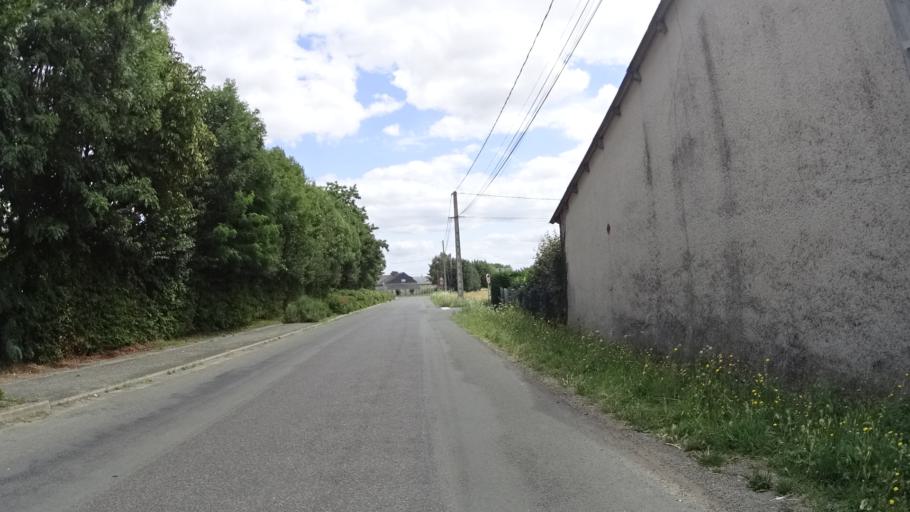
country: FR
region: Pays de la Loire
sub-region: Departement de Maine-et-Loire
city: La Menitre
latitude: 47.4049
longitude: -0.2609
